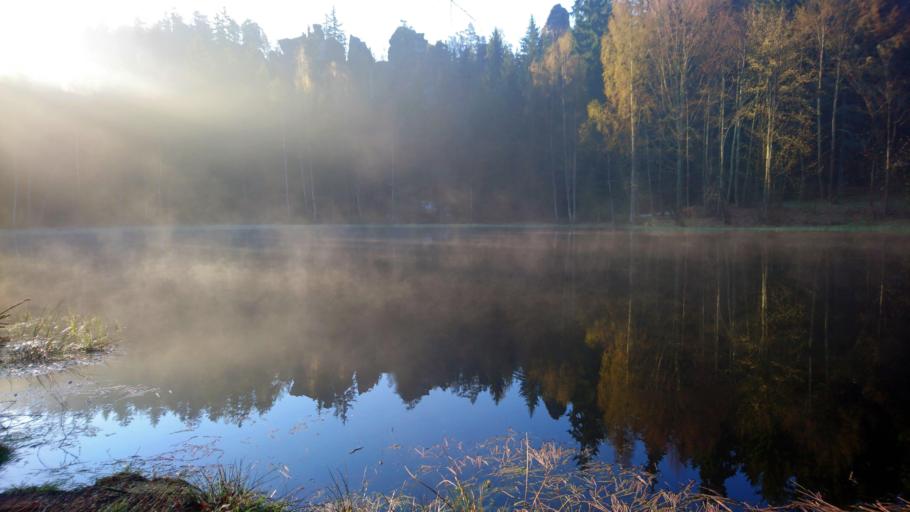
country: CZ
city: Teplice nad Metuji
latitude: 50.5732
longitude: 16.1403
